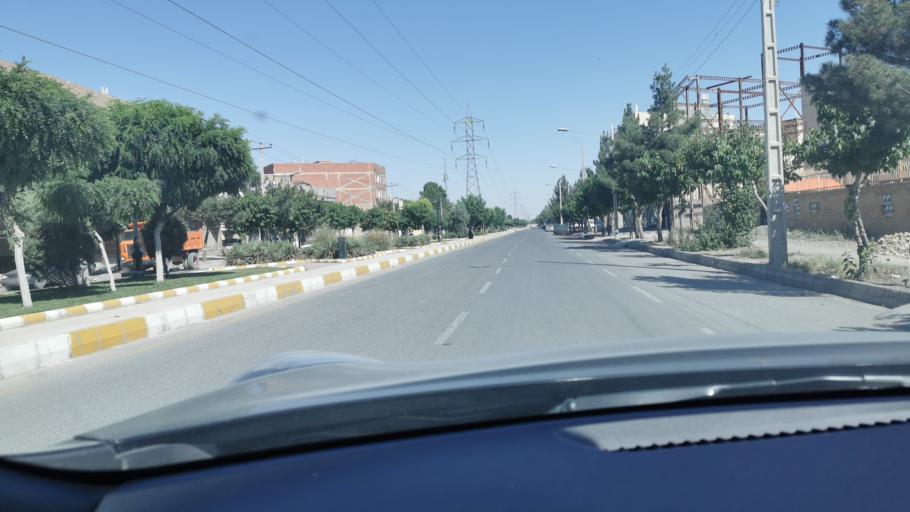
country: IR
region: Razavi Khorasan
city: Chenaran
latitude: 36.6389
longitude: 59.1173
